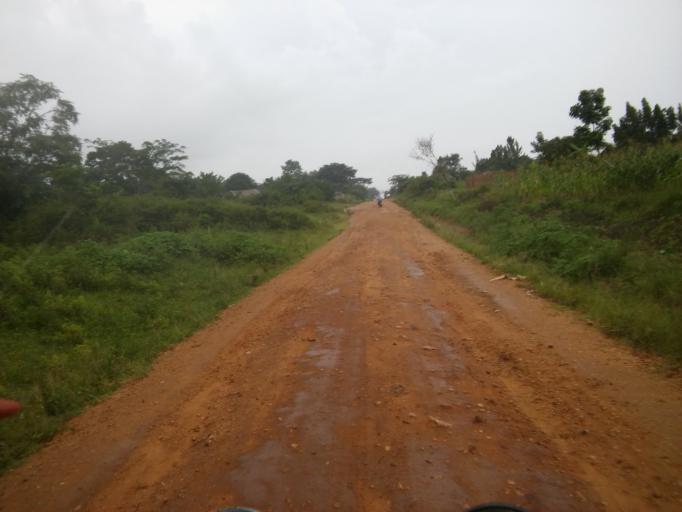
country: UG
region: Eastern Region
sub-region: Mbale District
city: Mbale
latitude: 0.9845
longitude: 34.2011
